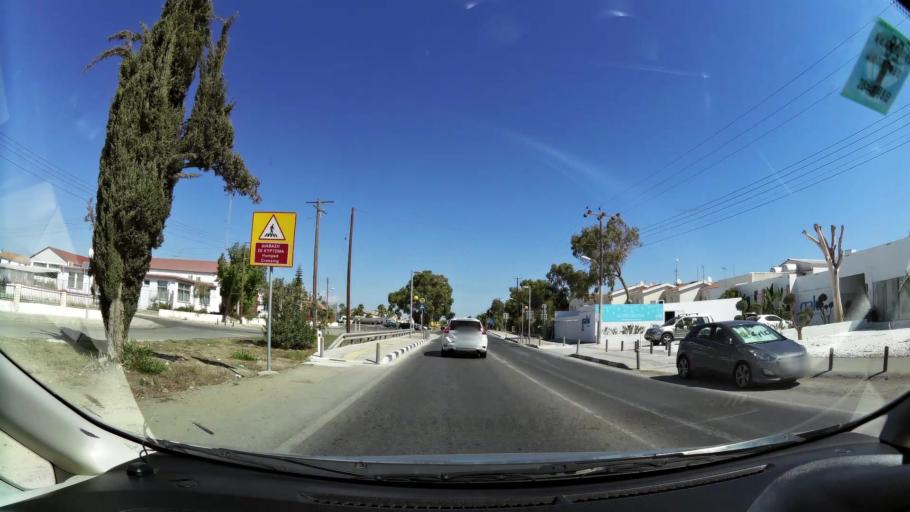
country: CY
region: Larnaka
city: Voroklini
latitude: 34.9602
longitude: 33.6572
